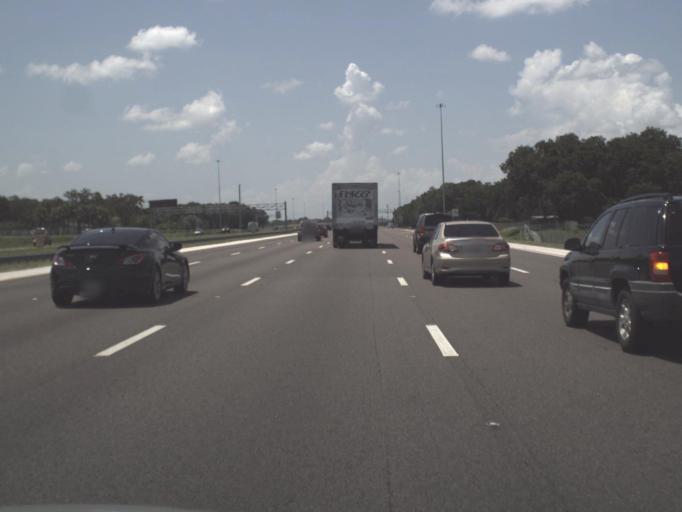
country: US
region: Florida
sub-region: Hillsborough County
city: Mango
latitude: 28.0002
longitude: -82.3360
